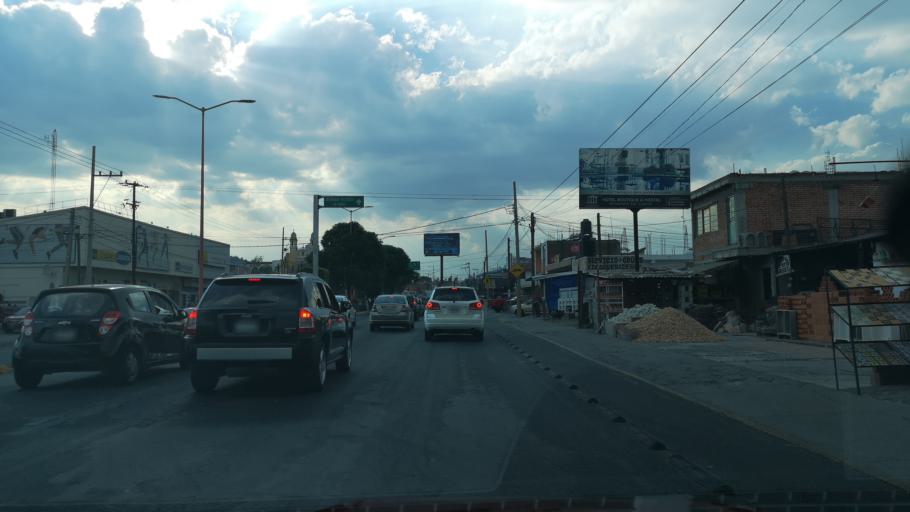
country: MX
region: Puebla
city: Cholula
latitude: 19.0708
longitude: -98.3137
